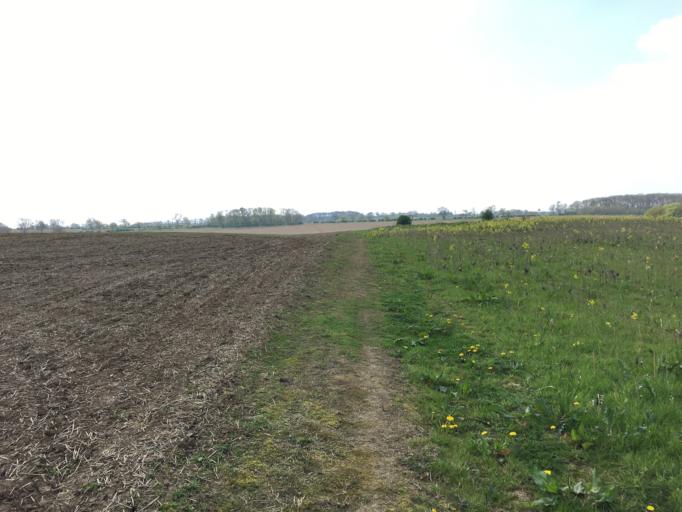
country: GB
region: England
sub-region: Leicestershire
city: Houghton on the Hill
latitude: 52.6157
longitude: -0.9955
